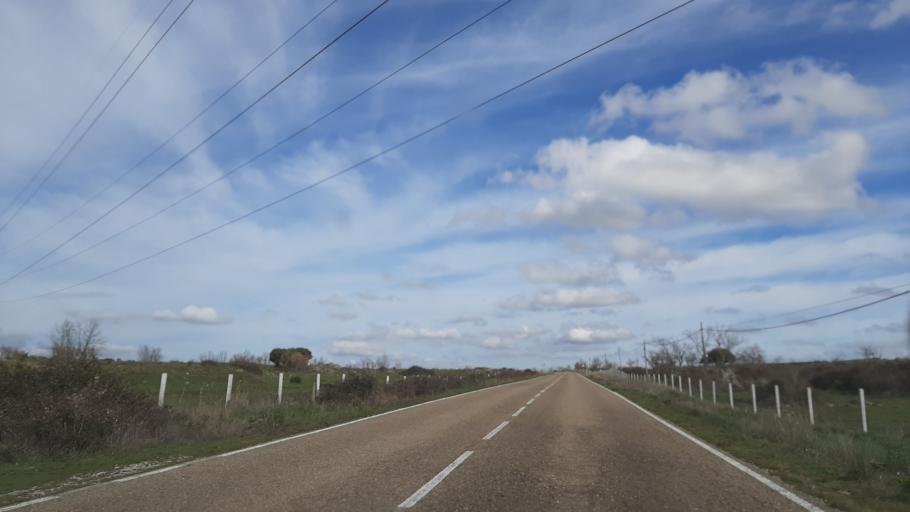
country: ES
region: Castille and Leon
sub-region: Provincia de Salamanca
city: Villarino de los Aires
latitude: 41.2442
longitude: -6.5058
